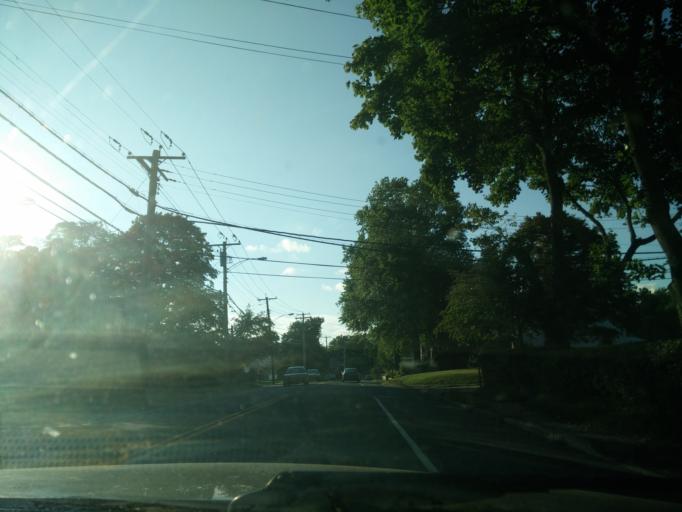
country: US
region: Connecticut
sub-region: Fairfield County
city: Bridgeport
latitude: 41.1740
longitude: -73.2372
